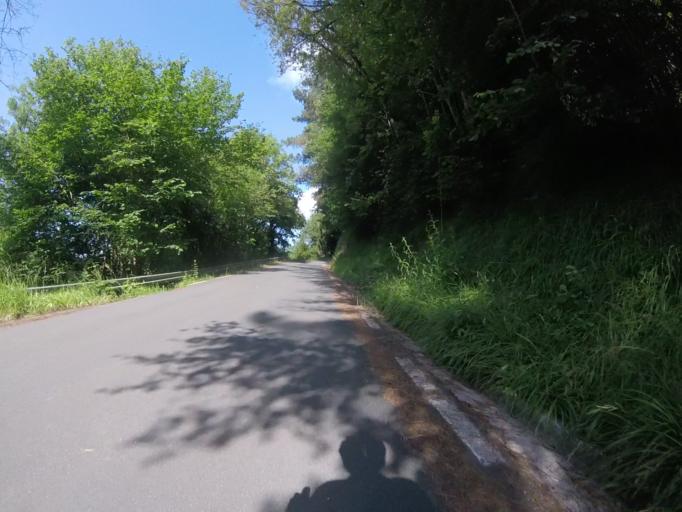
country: ES
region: Basque Country
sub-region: Provincia de Guipuzcoa
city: Beasain
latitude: 43.0768
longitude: -2.2215
